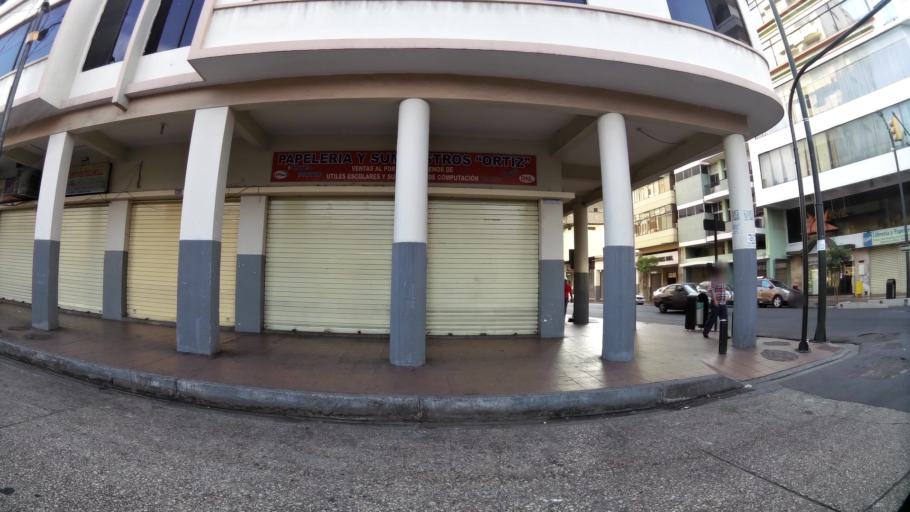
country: EC
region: Guayas
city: Guayaquil
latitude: -2.1934
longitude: -79.8875
